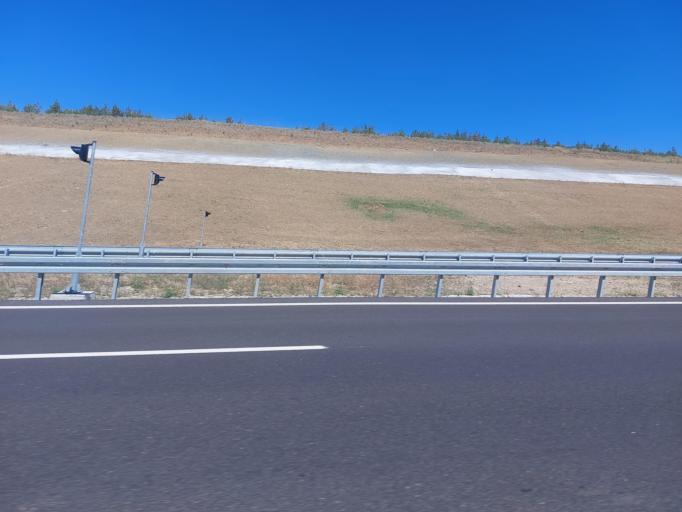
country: TR
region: Canakkale
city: Evrese
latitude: 40.7129
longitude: 26.9834
